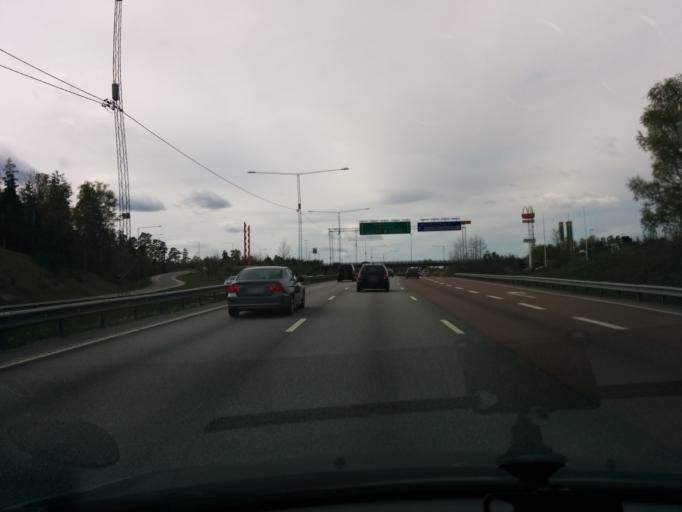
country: SE
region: Stockholm
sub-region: Huddinge Kommun
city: Segeltorp
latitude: 59.2655
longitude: 17.9002
